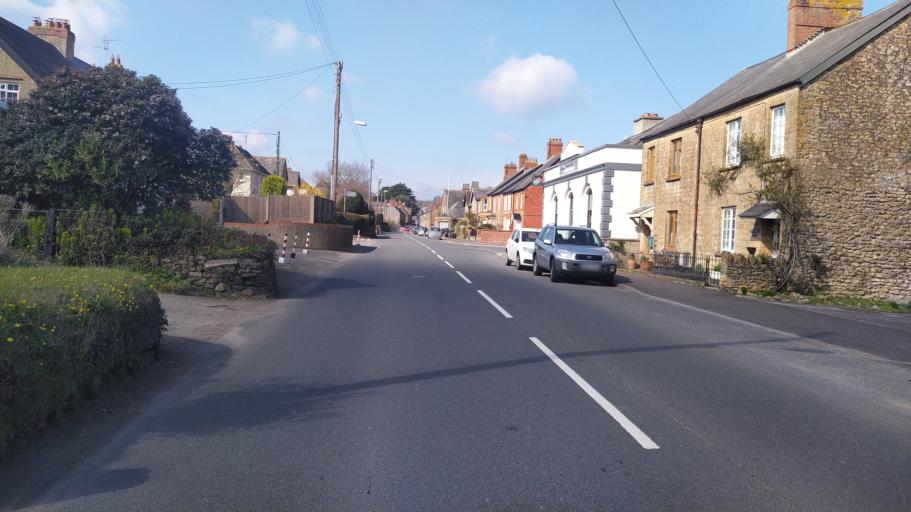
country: GB
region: England
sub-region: Somerset
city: Crewkerne
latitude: 50.8809
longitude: -2.7885
